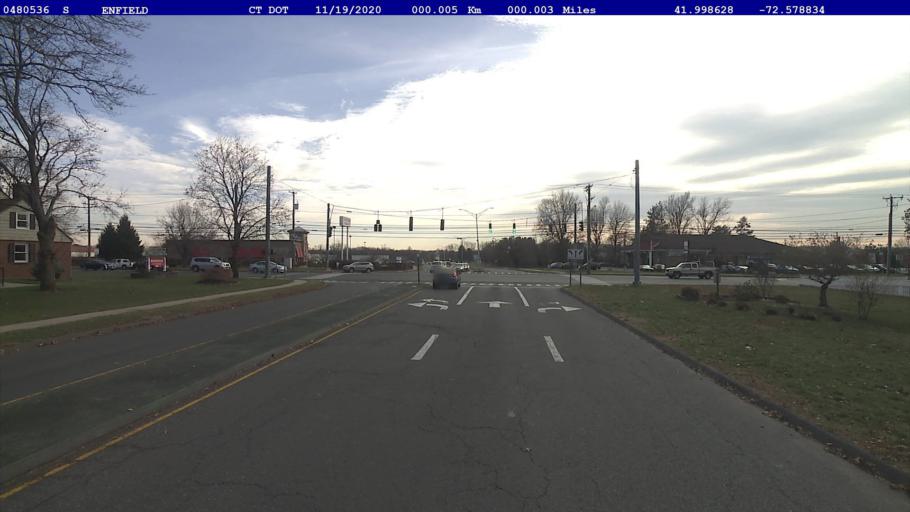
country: US
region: Connecticut
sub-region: Hartford County
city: Thompsonville
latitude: 41.9986
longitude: -72.5788
